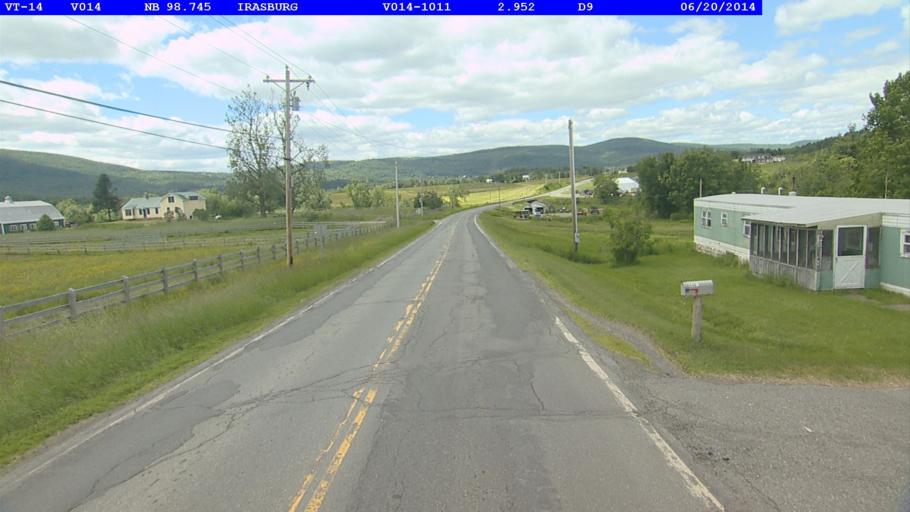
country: US
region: Vermont
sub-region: Orleans County
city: Newport
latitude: 44.8058
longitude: -72.2829
